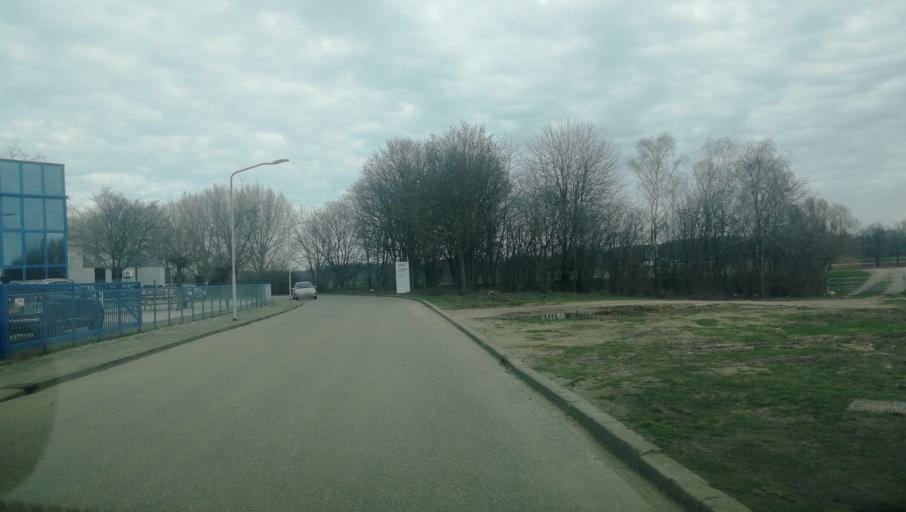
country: NL
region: Limburg
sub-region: Gemeente Venlo
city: Venlo
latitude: 51.3837
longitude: 6.1583
